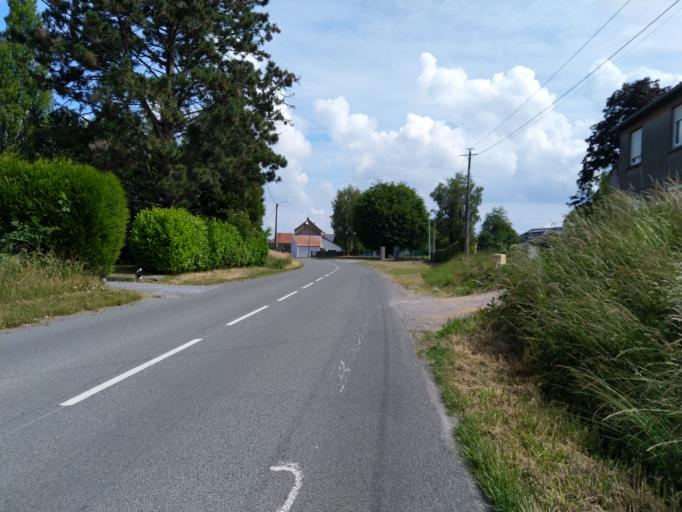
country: FR
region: Nord-Pas-de-Calais
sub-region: Departement du Nord
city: Rousies
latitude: 50.2943
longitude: 3.9914
